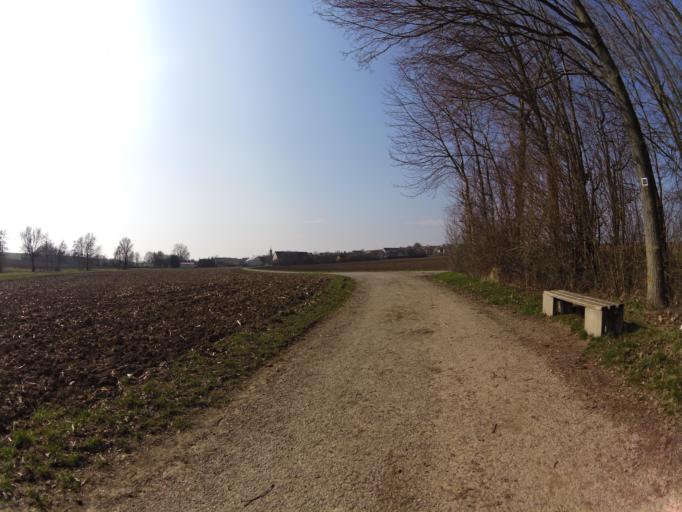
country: DE
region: Bavaria
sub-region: Regierungsbezirk Unterfranken
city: Sulzdorf
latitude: 49.6499
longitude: 9.9125
